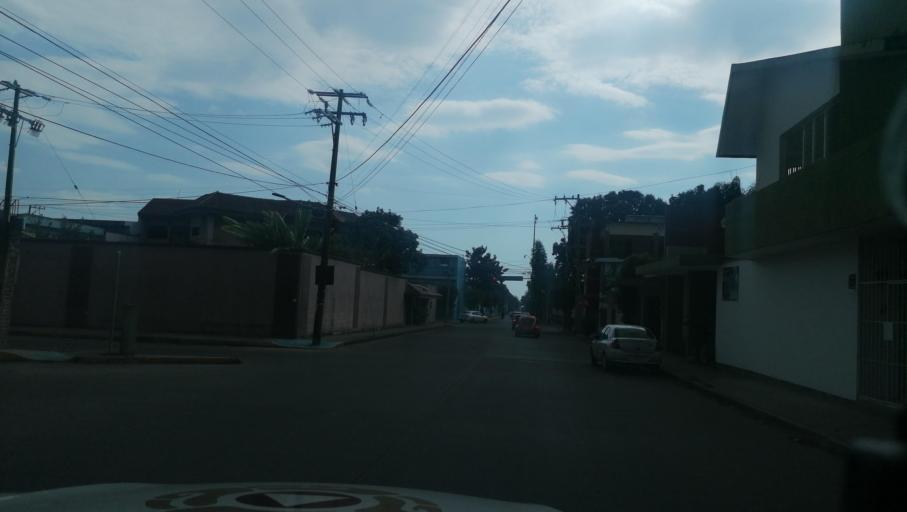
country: MX
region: Chiapas
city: Tapachula
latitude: 14.9179
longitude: -92.2525
